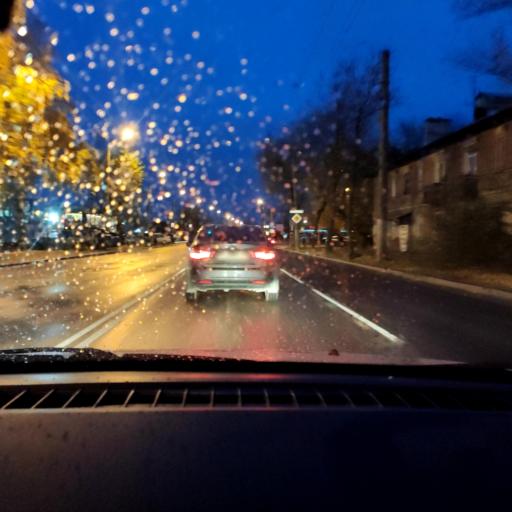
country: RU
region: Perm
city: Perm
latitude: 57.9738
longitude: 56.2463
